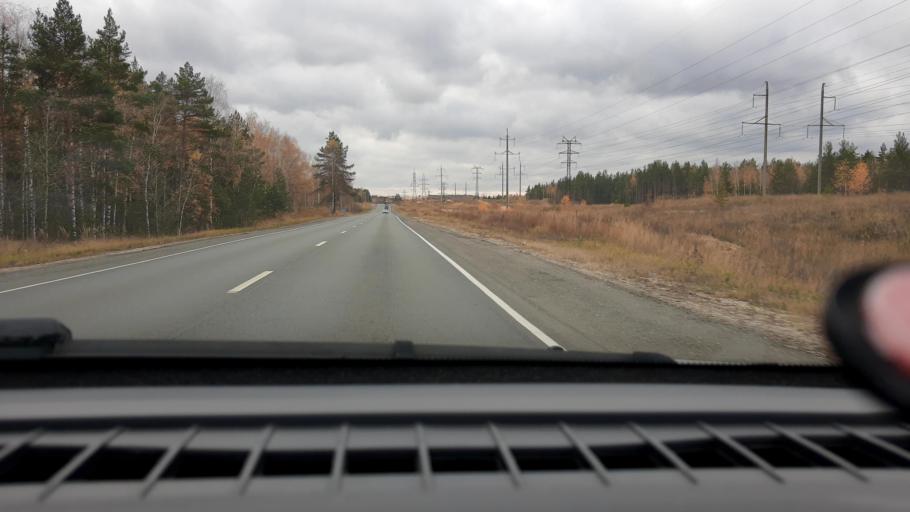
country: RU
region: Nizjnij Novgorod
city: Lukino
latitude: 56.3459
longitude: 43.5842
